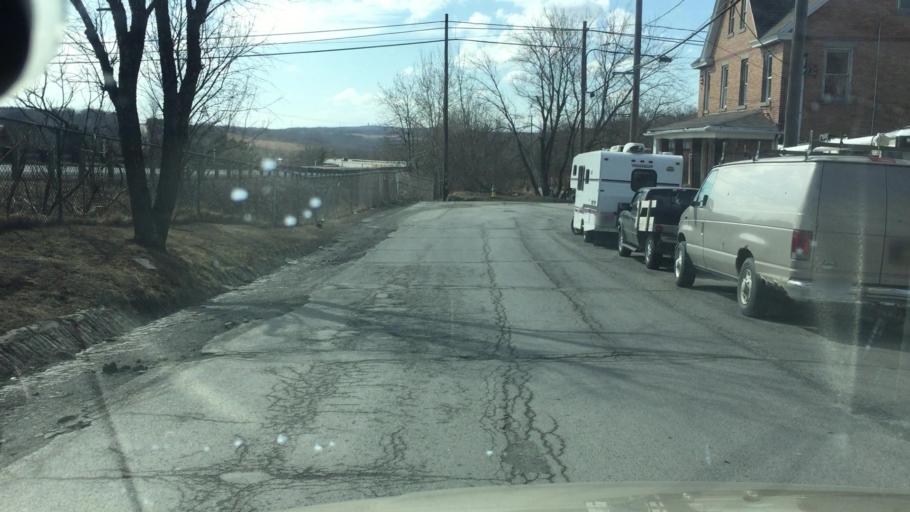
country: US
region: Pennsylvania
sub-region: Luzerne County
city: West Hazleton
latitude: 40.9564
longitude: -75.9959
